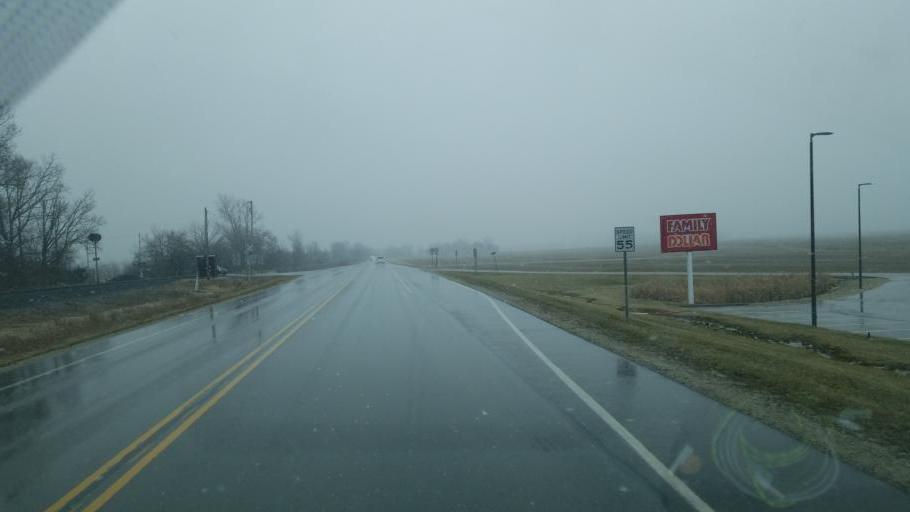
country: US
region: Indiana
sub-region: Wabash County
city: Mount Vernon
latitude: 40.6679
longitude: -85.7210
